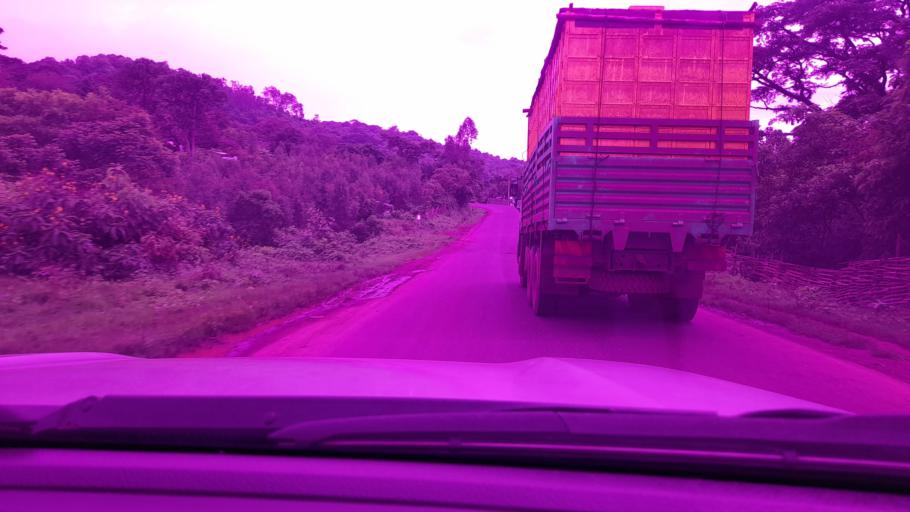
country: ET
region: Oromiya
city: Jima
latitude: 7.6598
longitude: 36.8791
